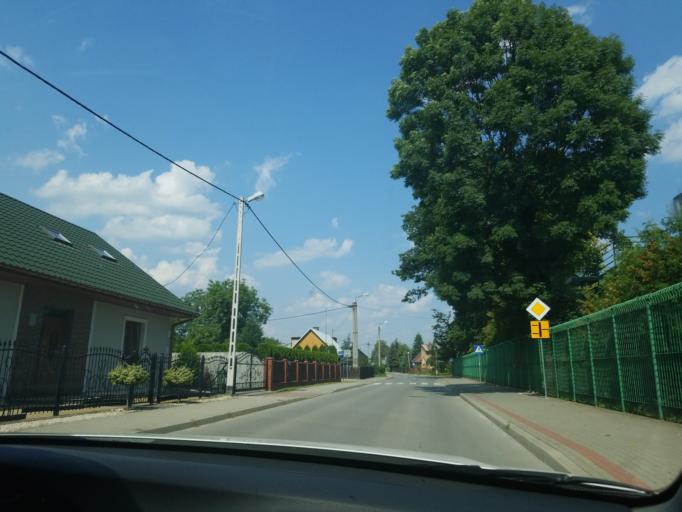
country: PL
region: Subcarpathian Voivodeship
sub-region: Powiat nizanski
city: Nisko
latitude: 50.5217
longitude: 22.1466
